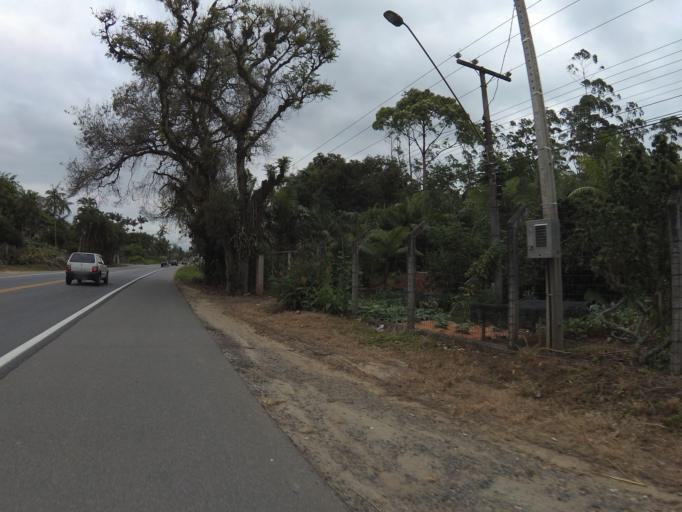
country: BR
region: Santa Catarina
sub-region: Blumenau
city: Blumenau
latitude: -26.8691
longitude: -49.1423
